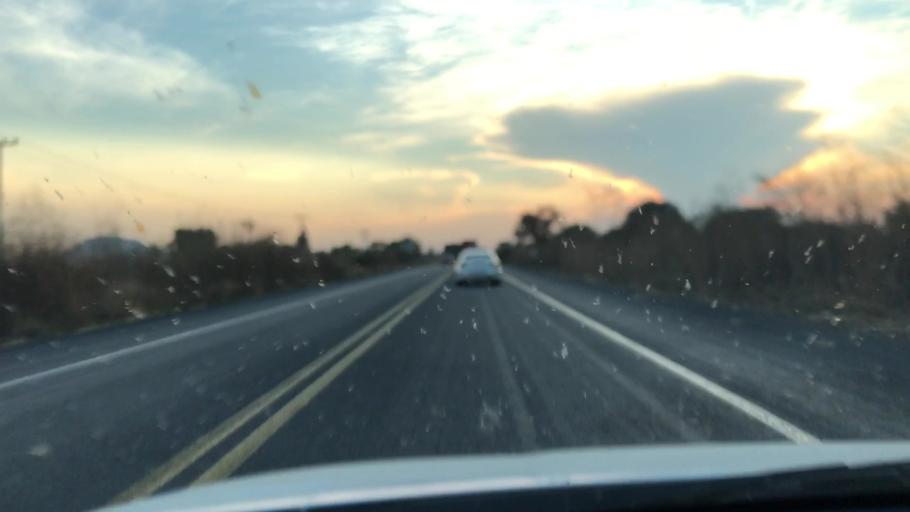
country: MX
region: Michoacan
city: Tanhuato de Guerrero
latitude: 20.3058
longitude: -102.3171
